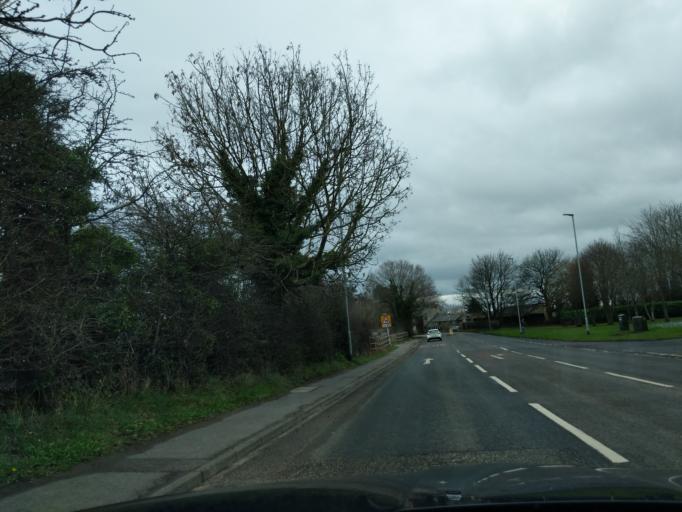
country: GB
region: England
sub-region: Northumberland
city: Morpeth
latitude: 55.1745
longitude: -1.7011
